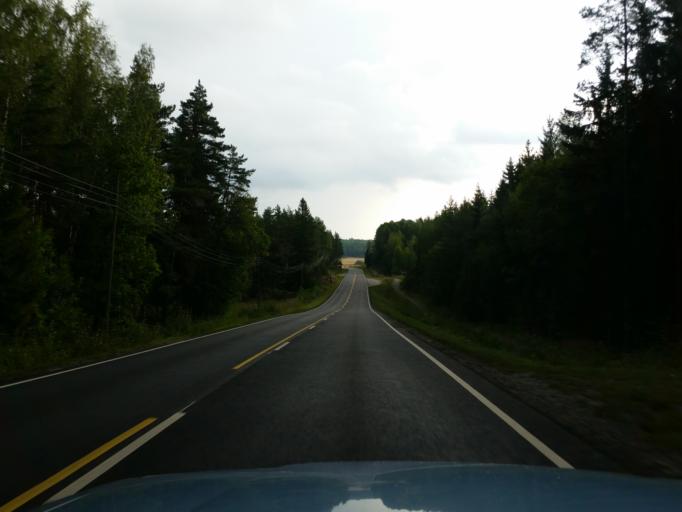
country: FI
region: Varsinais-Suomi
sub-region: Aboland-Turunmaa
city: Laensi-Turunmaa
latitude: 60.2740
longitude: 22.2262
